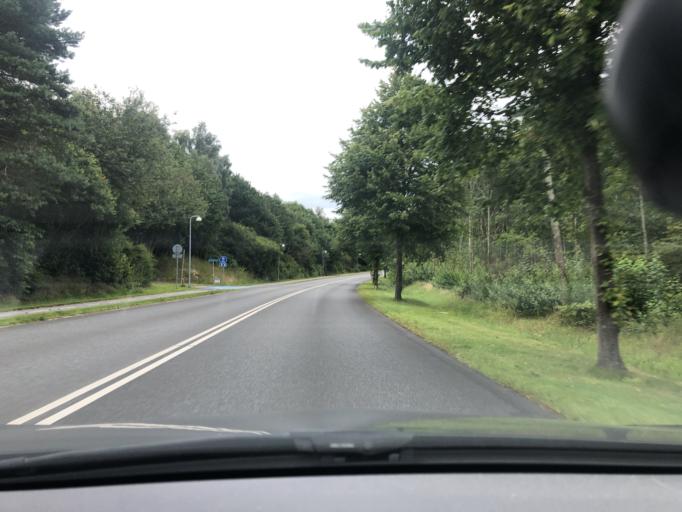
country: DK
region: South Denmark
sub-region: Vejle Kommune
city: Vejle
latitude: 55.6723
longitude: 9.5439
